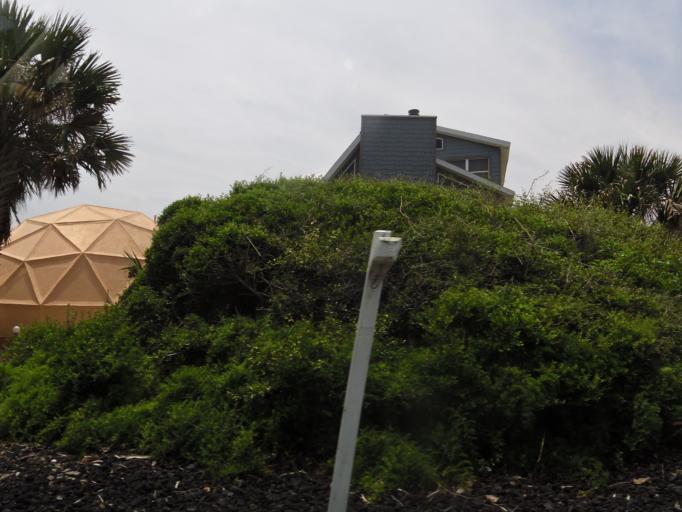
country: US
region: Florida
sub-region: Flagler County
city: Flagler Beach
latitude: 29.4467
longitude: -81.1122
